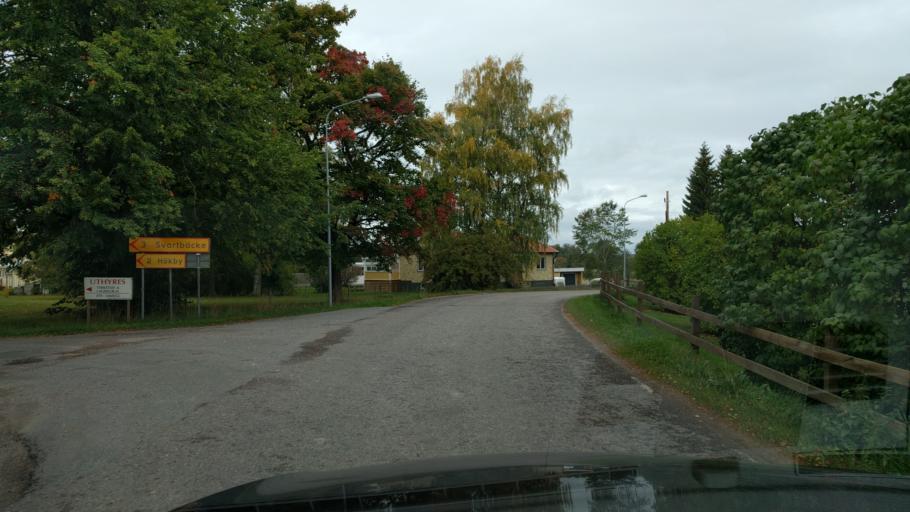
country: SE
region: Uppsala
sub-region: Osthammars Kommun
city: Bjorklinge
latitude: 60.1446
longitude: 17.5756
